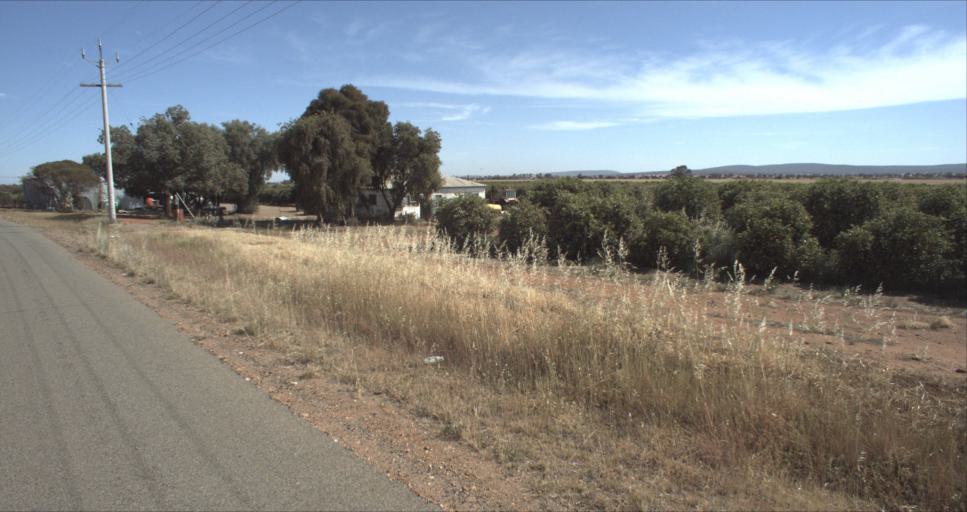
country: AU
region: New South Wales
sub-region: Leeton
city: Leeton
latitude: -34.5780
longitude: 146.4849
